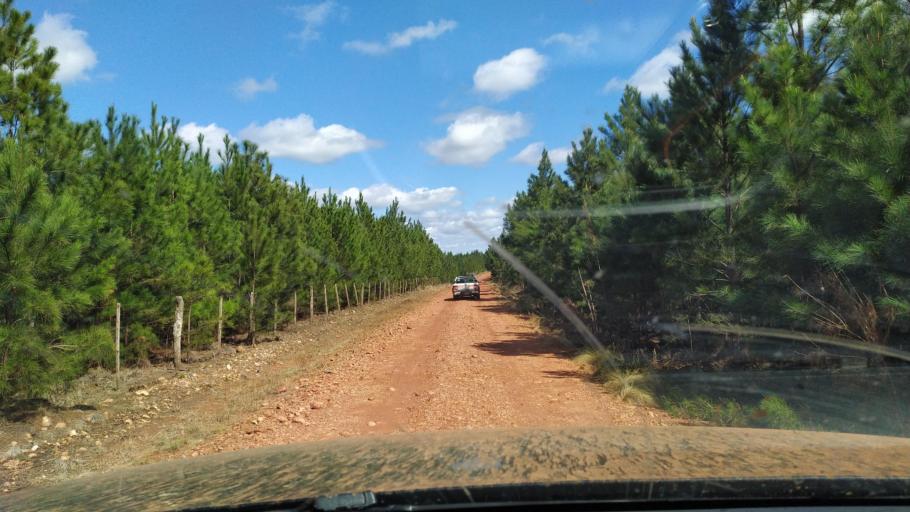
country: AR
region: Corrientes
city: Santo Tome
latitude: -28.4659
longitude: -55.9781
